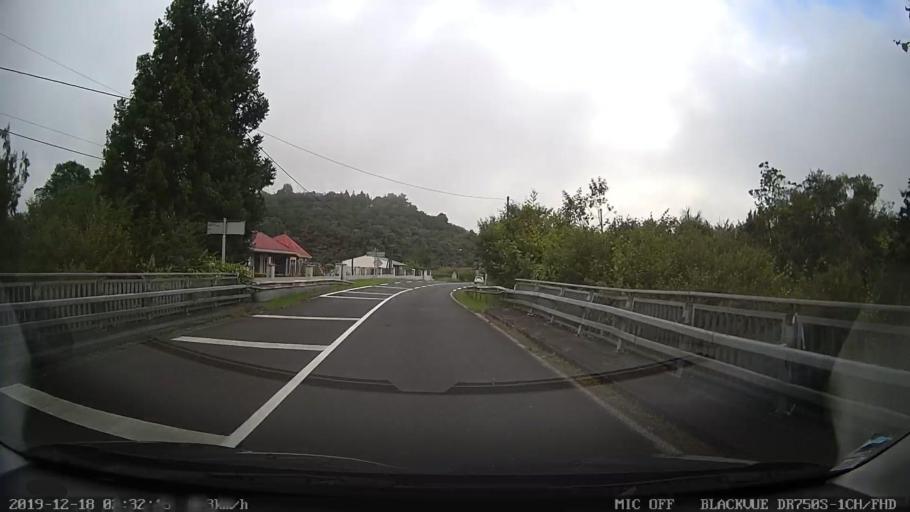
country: RE
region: Reunion
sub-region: Reunion
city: Cilaos
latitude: -21.1562
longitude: 55.6084
